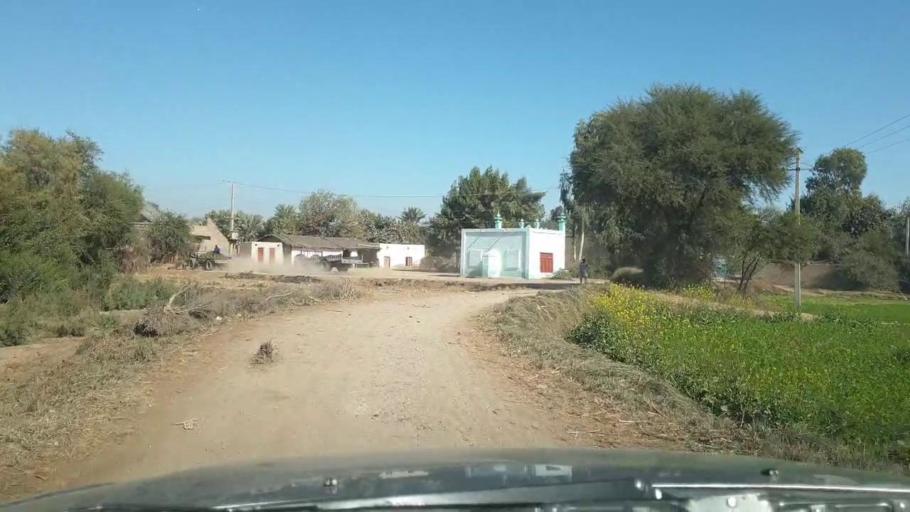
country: PK
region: Sindh
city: Ghotki
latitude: 28.0519
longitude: 69.2293
